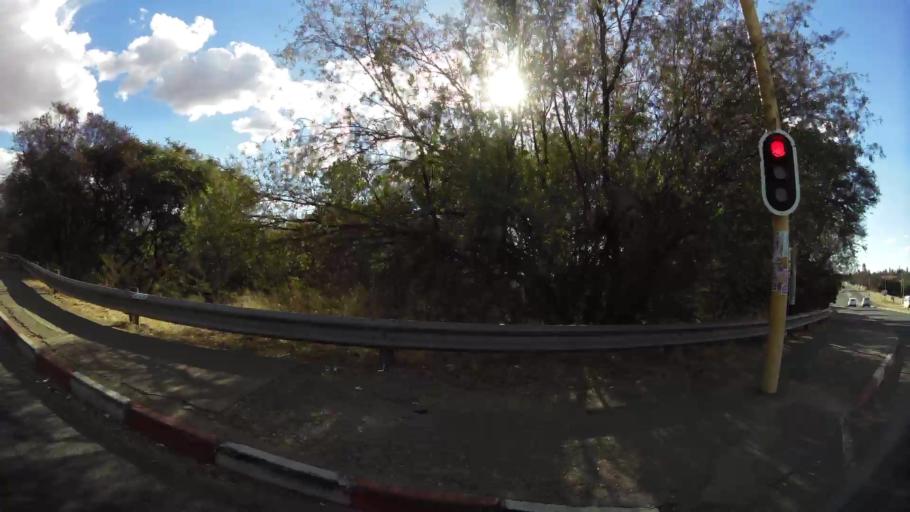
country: ZA
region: North-West
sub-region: Dr Kenneth Kaunda District Municipality
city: Klerksdorp
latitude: -26.8601
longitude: 26.6651
